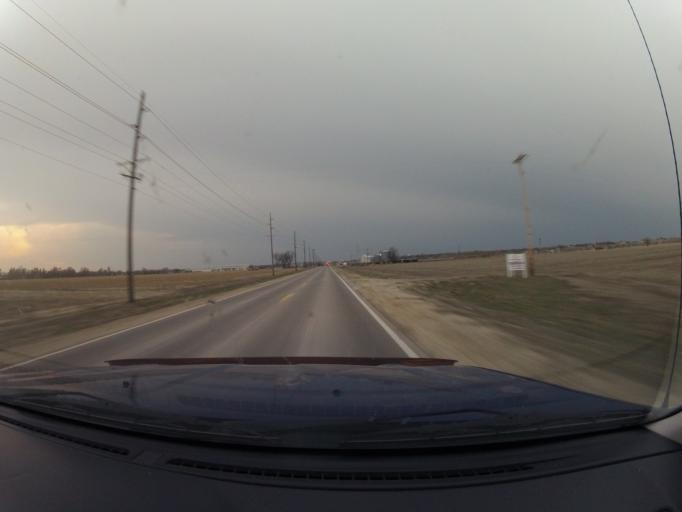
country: US
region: Nebraska
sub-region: Buffalo County
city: Kearney
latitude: 40.7138
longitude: -99.0496
